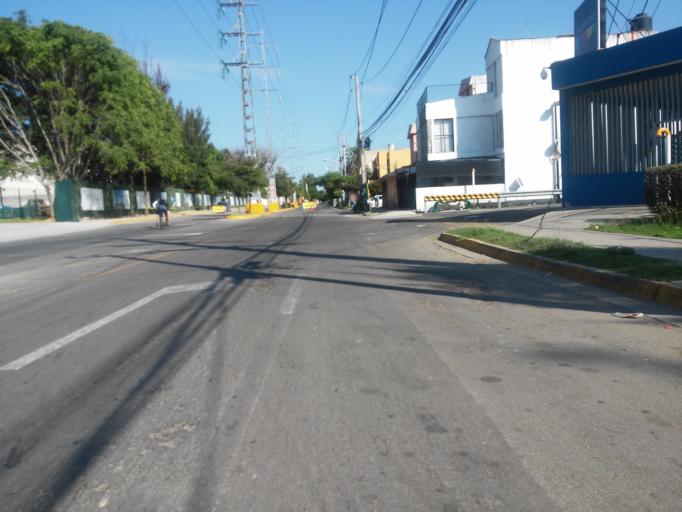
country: MX
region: Jalisco
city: Guadalajara
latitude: 20.6478
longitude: -103.4178
